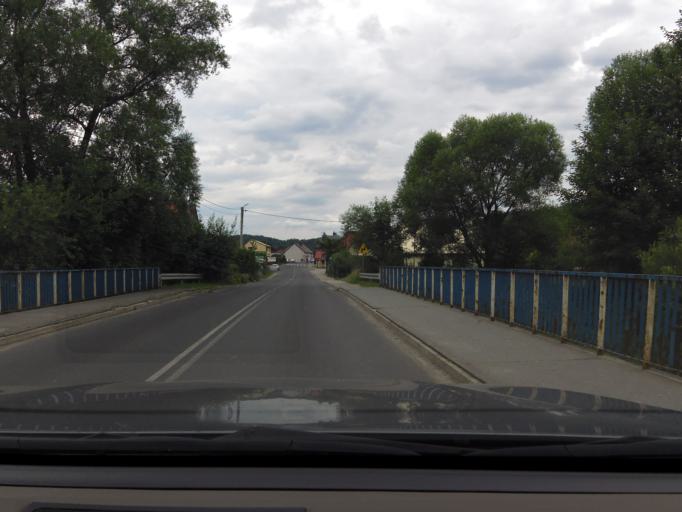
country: PL
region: Silesian Voivodeship
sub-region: Powiat zywiecki
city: Ujsoly
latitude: 49.4797
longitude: 19.1415
